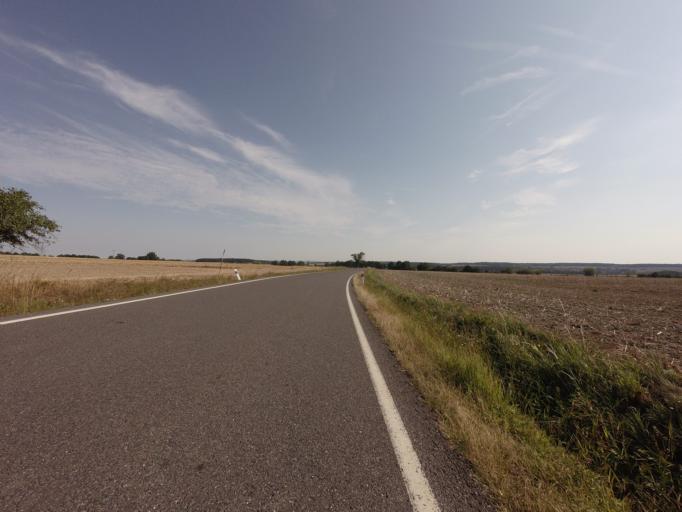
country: CZ
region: Jihocesky
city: Bernartice
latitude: 49.3355
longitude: 14.3631
